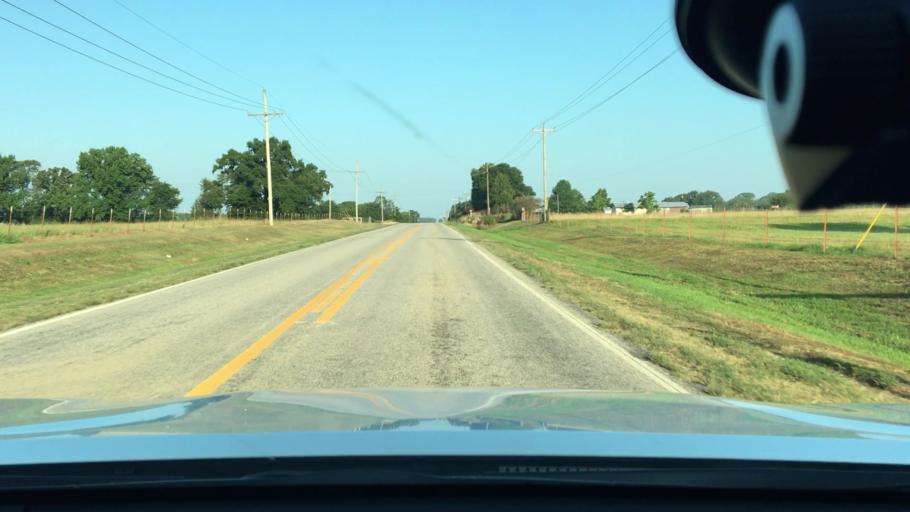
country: US
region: Arkansas
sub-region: Johnson County
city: Coal Hill
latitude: 35.3370
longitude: -93.6074
